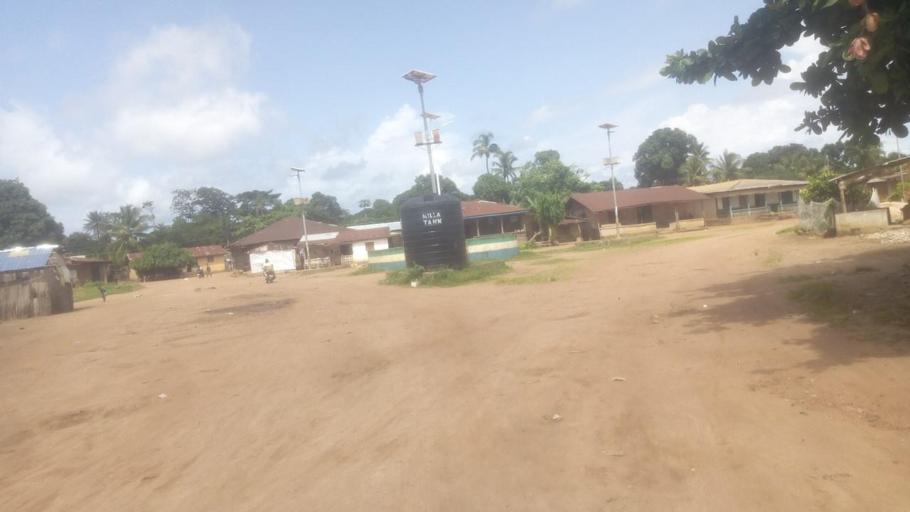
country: SL
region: Northern Province
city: Tintafor
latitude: 8.6410
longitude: -13.2274
